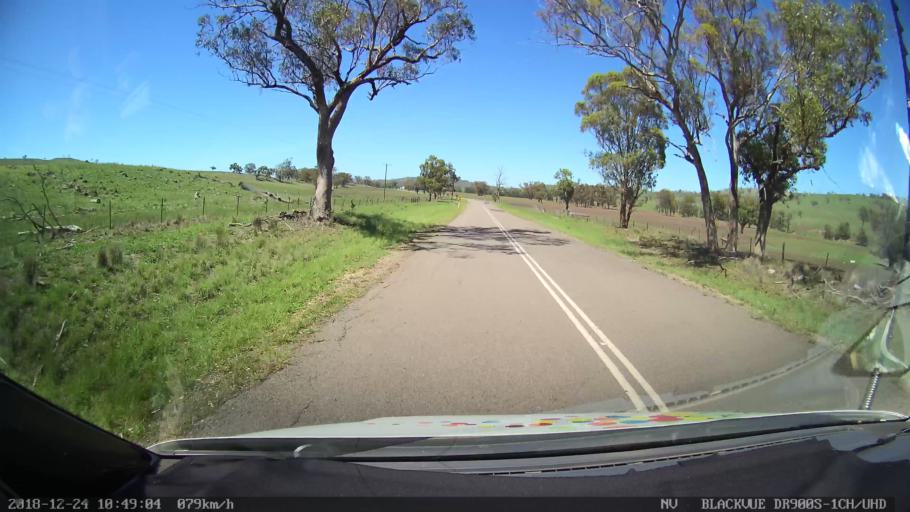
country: AU
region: New South Wales
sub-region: Upper Hunter Shire
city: Merriwa
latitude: -31.9431
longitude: 150.4294
